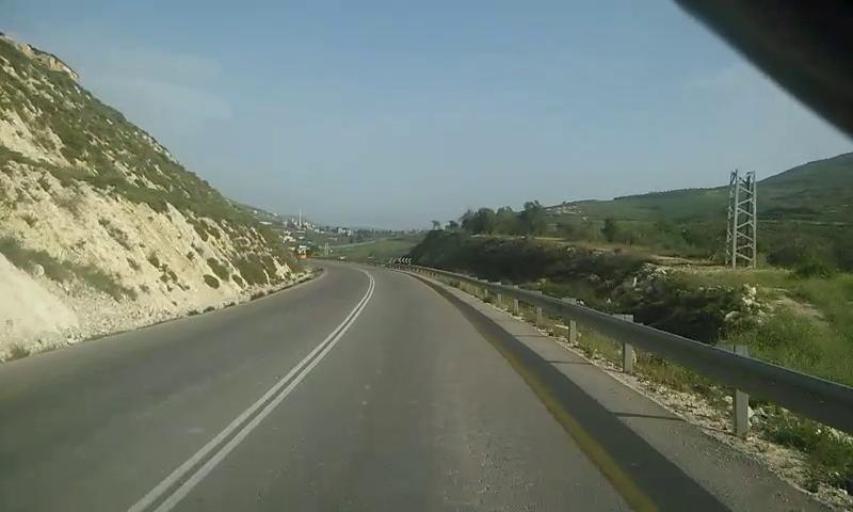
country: PS
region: West Bank
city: Madama
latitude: 32.1852
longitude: 35.2348
